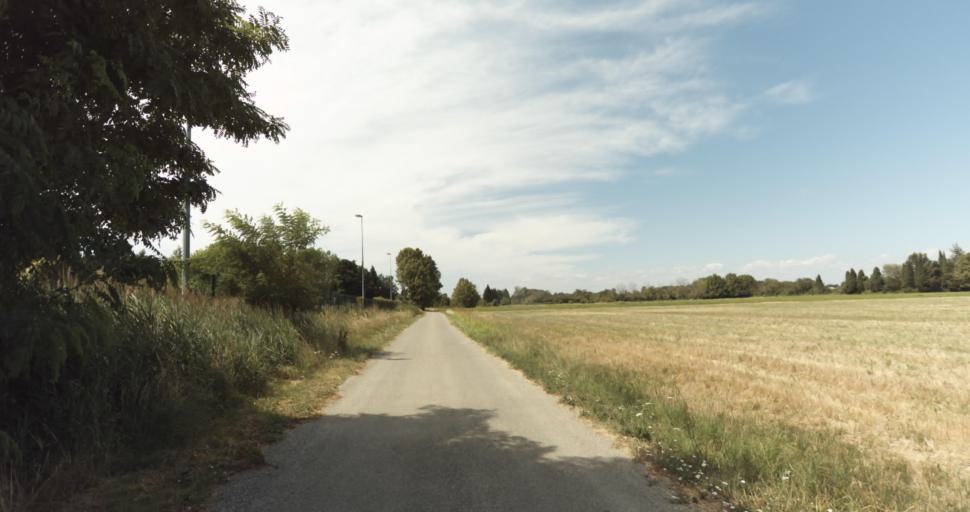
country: FR
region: Provence-Alpes-Cote d'Azur
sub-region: Departement du Vaucluse
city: Althen-des-Paluds
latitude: 44.0263
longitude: 4.9632
